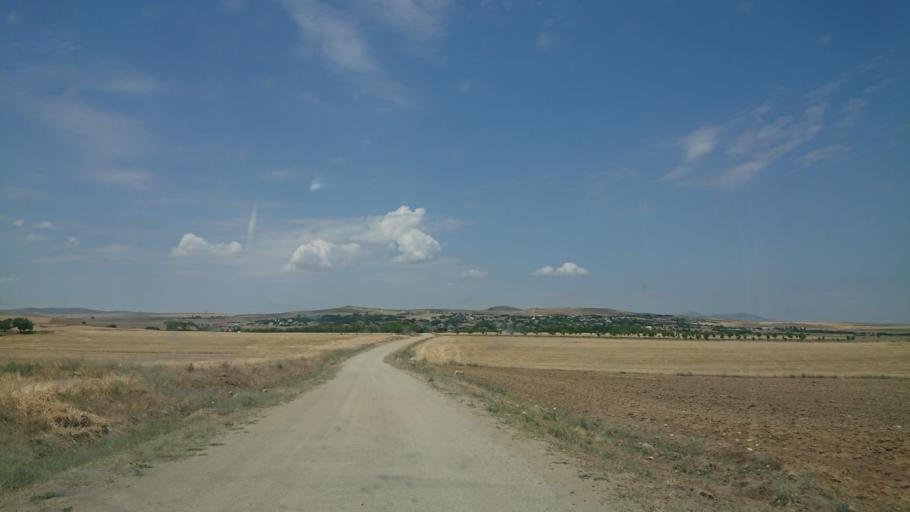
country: TR
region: Aksaray
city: Sariyahsi
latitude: 38.9571
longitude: 33.9028
